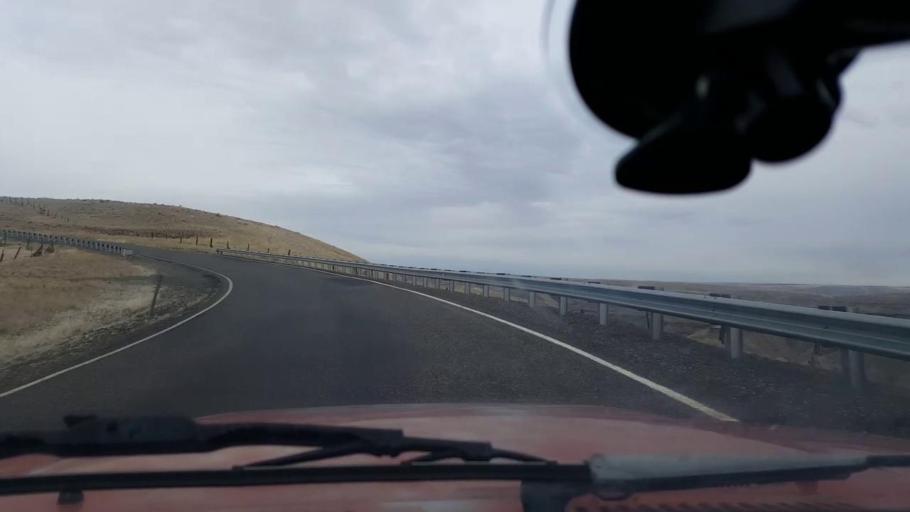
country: US
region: Washington
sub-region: Asotin County
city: Clarkston Heights-Vineland
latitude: 46.3346
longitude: -117.2992
